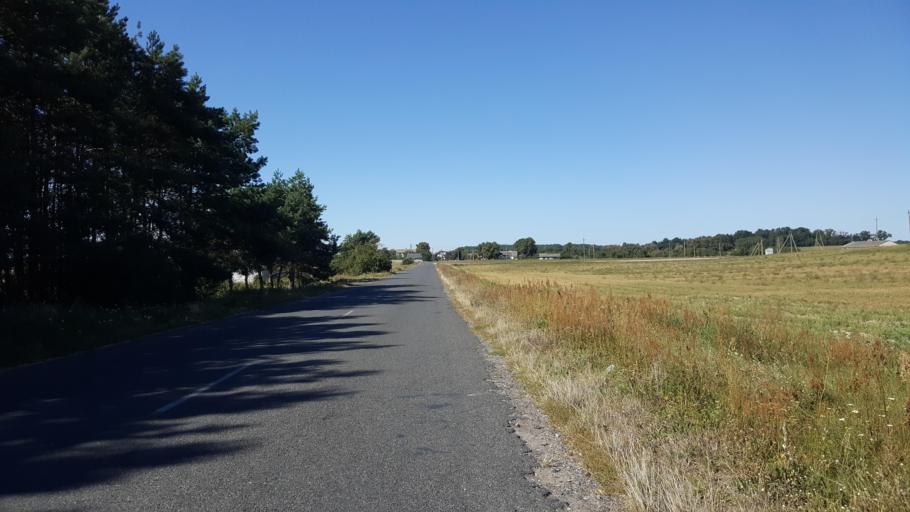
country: PL
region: Lublin Voivodeship
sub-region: Powiat bialski
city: Terespol
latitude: 52.2121
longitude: 23.5200
